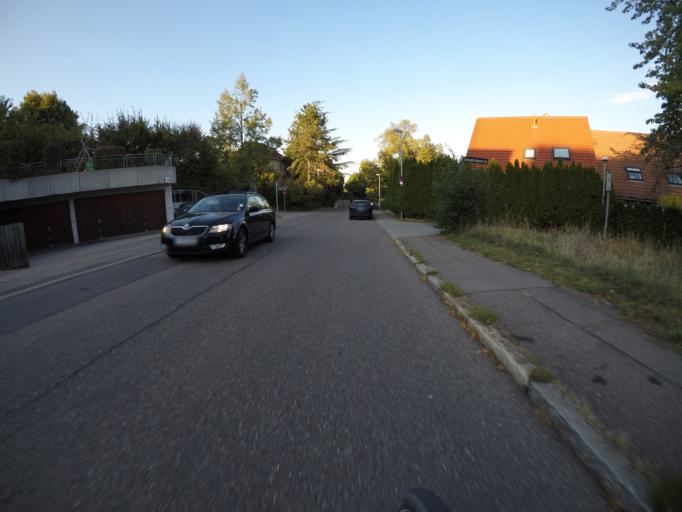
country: DE
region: Baden-Wuerttemberg
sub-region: Regierungsbezirk Stuttgart
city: Ostfildern
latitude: 48.7503
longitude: 9.2407
